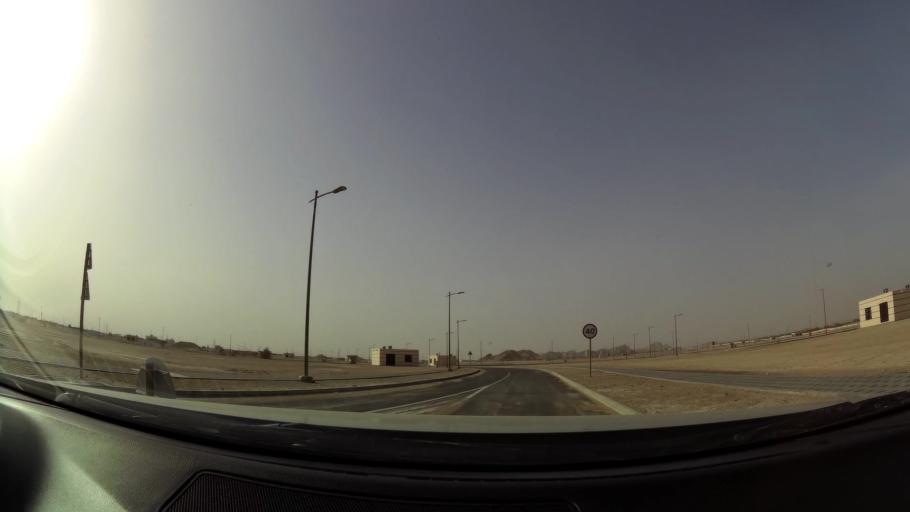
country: AE
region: Abu Dhabi
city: Al Ain
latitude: 24.1143
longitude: 55.7261
